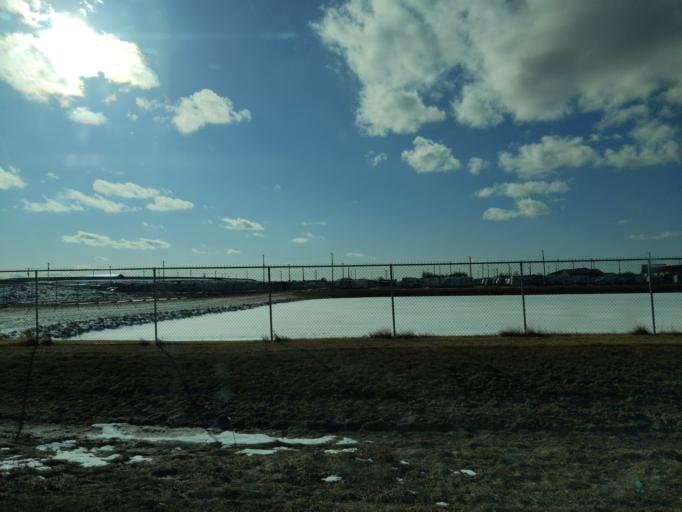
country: CA
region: Saskatchewan
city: Lloydminster
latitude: 53.2470
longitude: -109.9708
